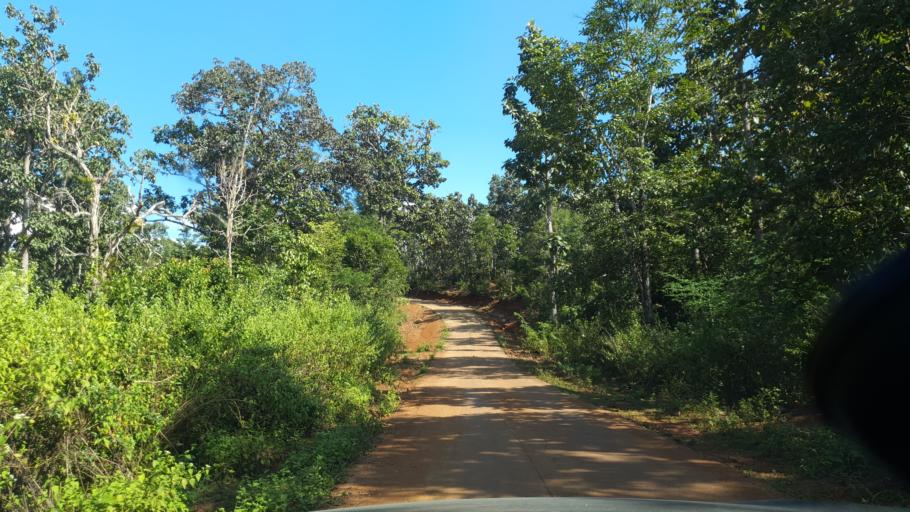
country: TH
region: Chiang Mai
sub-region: Amphoe Chiang Dao
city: Chiang Dao
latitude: 19.2964
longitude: 98.7134
